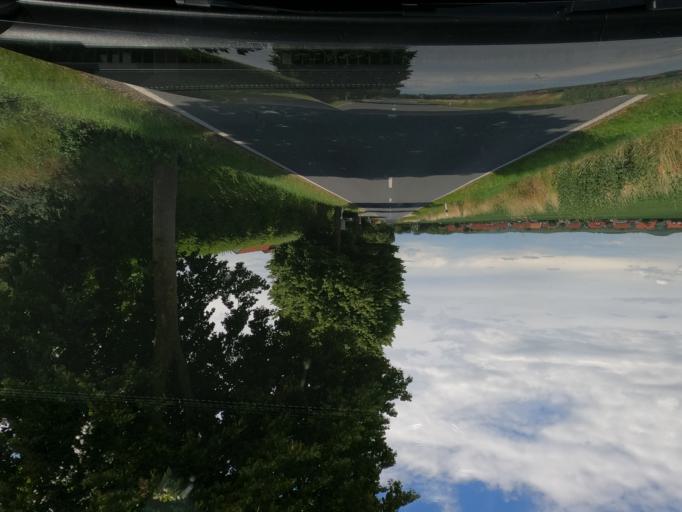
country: DE
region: Lower Saxony
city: Lengede
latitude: 52.1865
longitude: 10.2734
